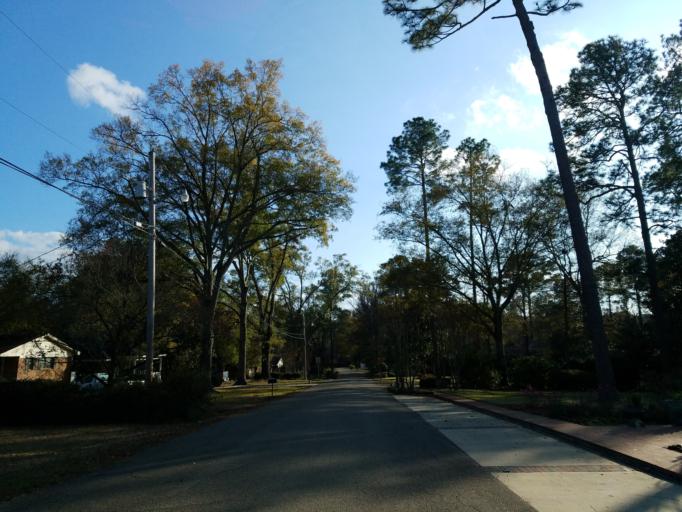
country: US
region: Mississippi
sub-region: Lamar County
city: West Hattiesburg
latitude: 31.3193
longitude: -89.3437
